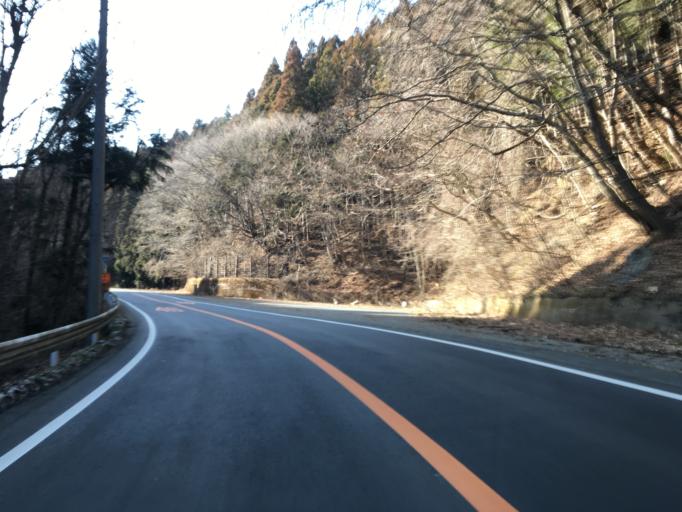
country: JP
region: Ibaraki
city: Takahagi
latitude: 36.7410
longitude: 140.5664
